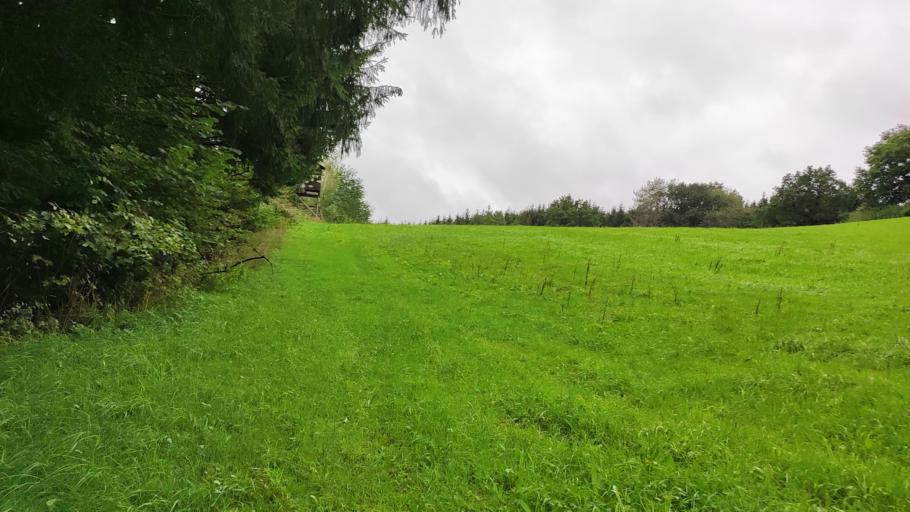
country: DE
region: Bavaria
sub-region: Swabia
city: Altenmunster
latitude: 48.4466
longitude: 10.6149
